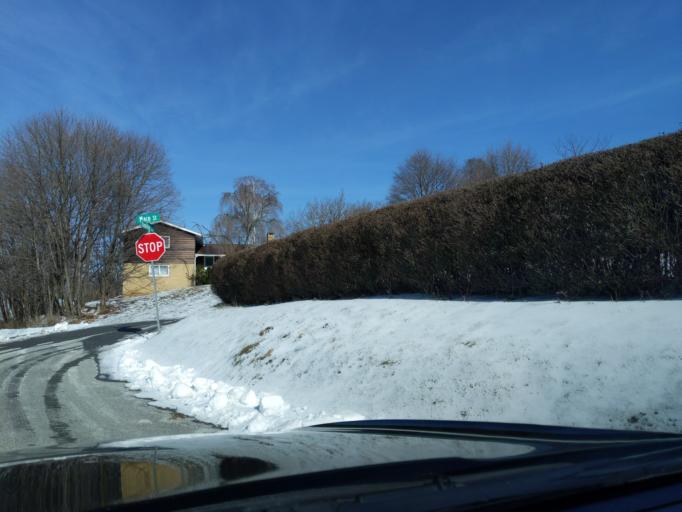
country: US
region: Pennsylvania
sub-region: Blair County
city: Greenwood
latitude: 40.5249
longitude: -78.3727
